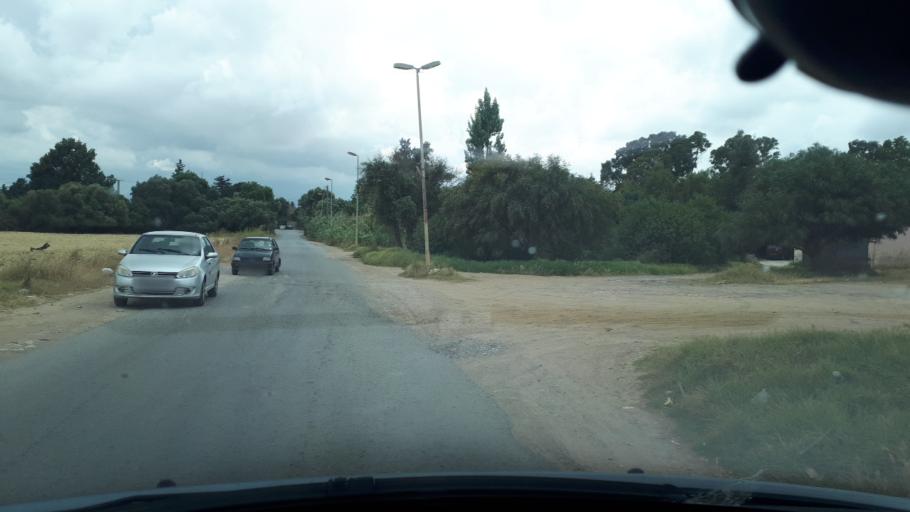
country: DZ
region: Tipaza
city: Cheraga
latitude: 36.7360
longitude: 2.9058
